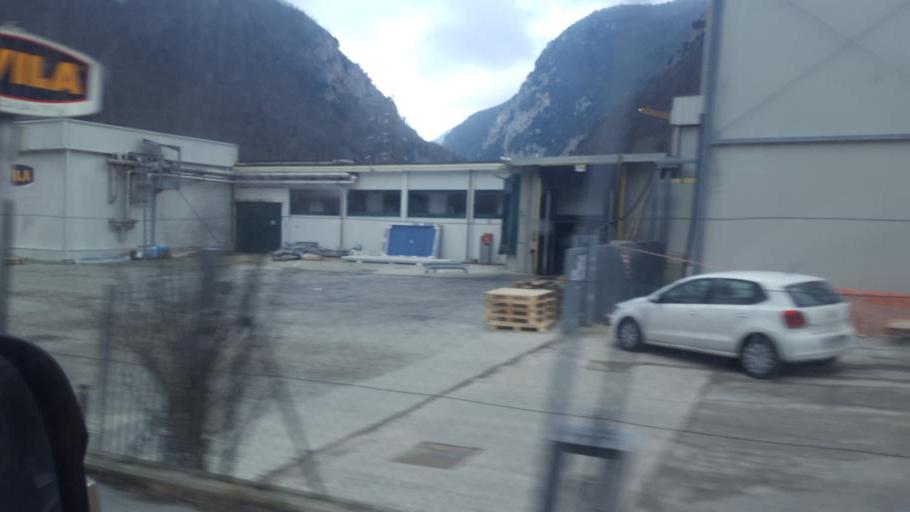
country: IT
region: The Marches
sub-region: Provincia di Macerata
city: Visso
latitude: 42.9350
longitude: 13.0820
